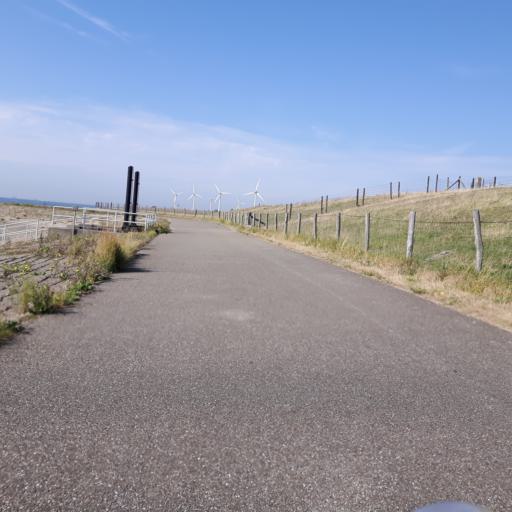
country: NL
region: Zeeland
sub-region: Gemeente Vlissingen
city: Vlissingen
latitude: 51.4417
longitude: 3.6232
